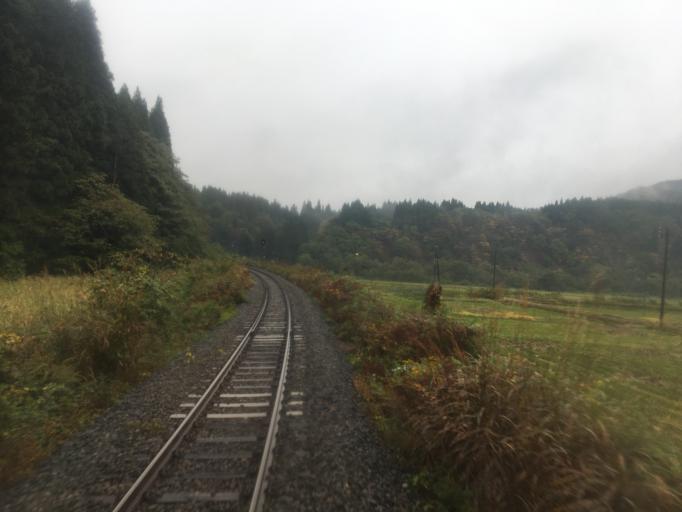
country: JP
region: Yamagata
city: Shinjo
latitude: 38.7364
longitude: 140.1342
